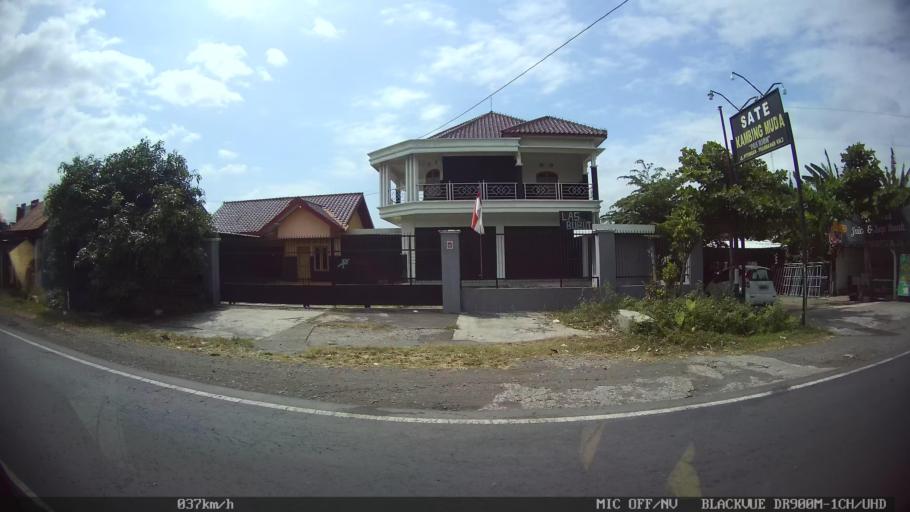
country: ID
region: Central Java
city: Candi Prambanan
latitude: -7.8238
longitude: 110.4800
